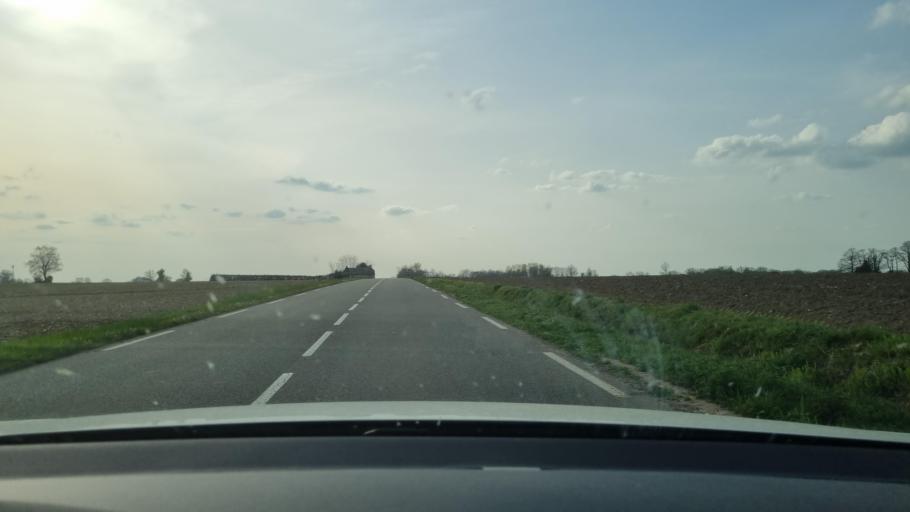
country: FR
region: Aquitaine
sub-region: Departement des Pyrenees-Atlantiques
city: Ger
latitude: 43.3760
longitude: -0.0898
